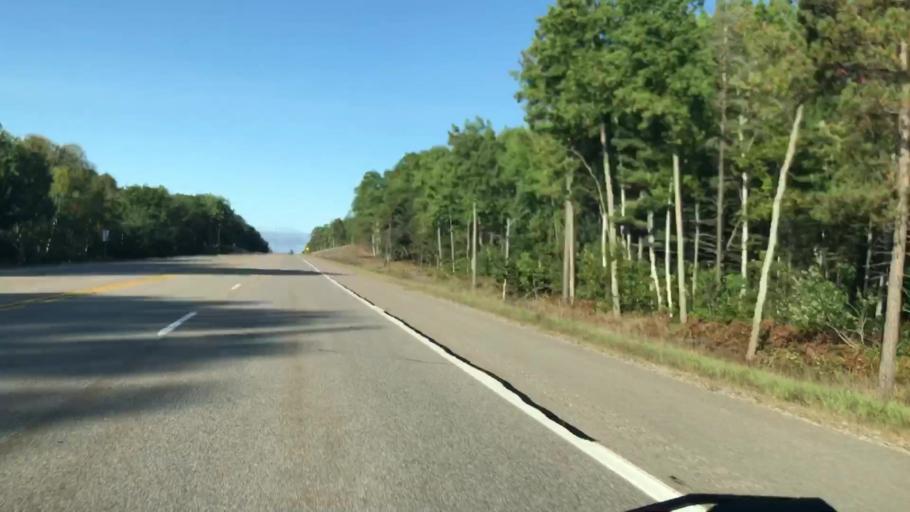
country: US
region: Michigan
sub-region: Chippewa County
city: Sault Ste. Marie
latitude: 46.3649
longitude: -84.7621
